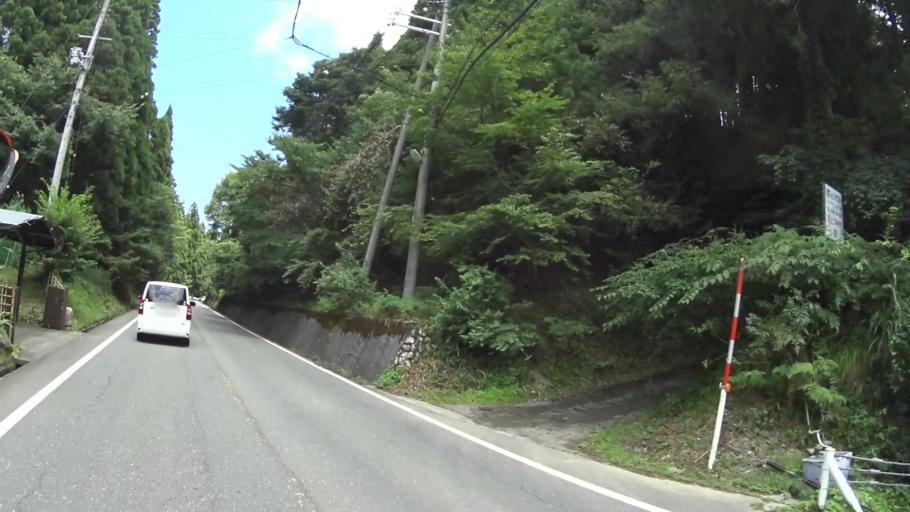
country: JP
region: Shiga Prefecture
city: Kitahama
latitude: 35.3056
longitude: 135.8894
